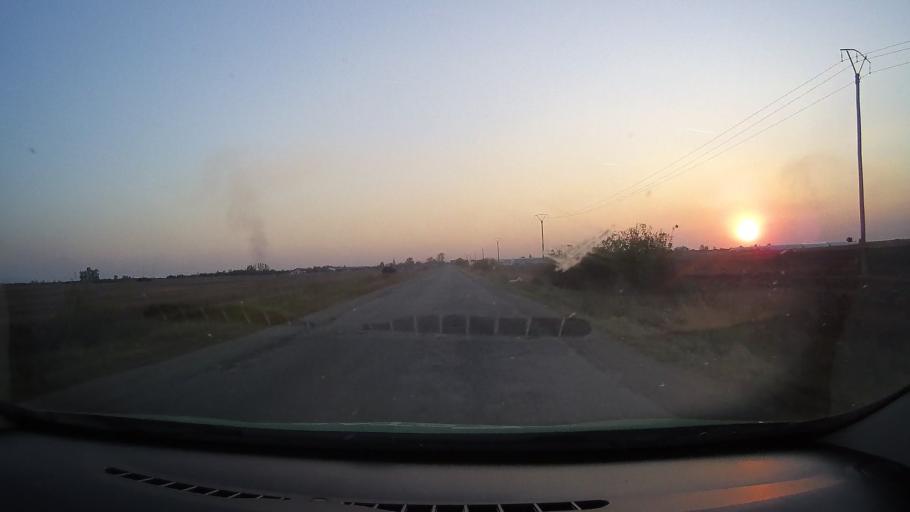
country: RO
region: Arad
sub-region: Comuna Olari
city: Olari
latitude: 46.3952
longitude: 21.5583
